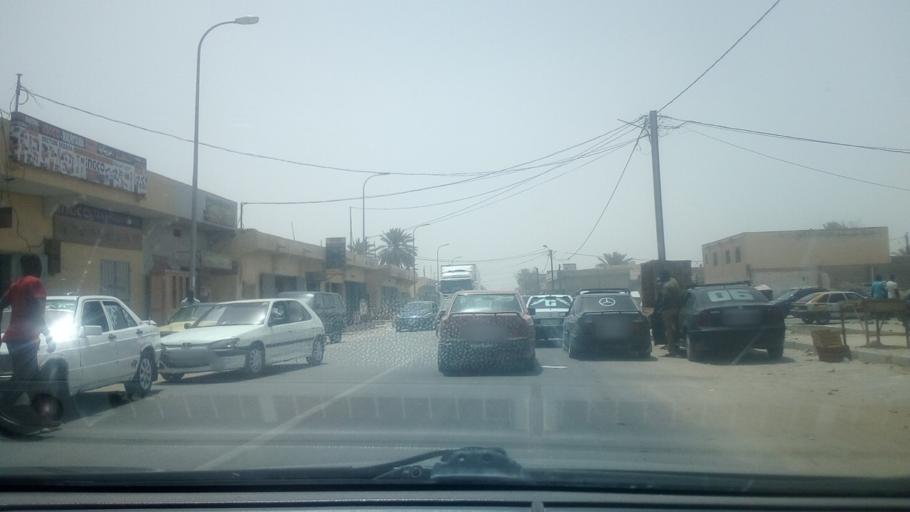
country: MR
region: Nouakchott
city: Nouakchott
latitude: 18.0813
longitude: -15.9888
